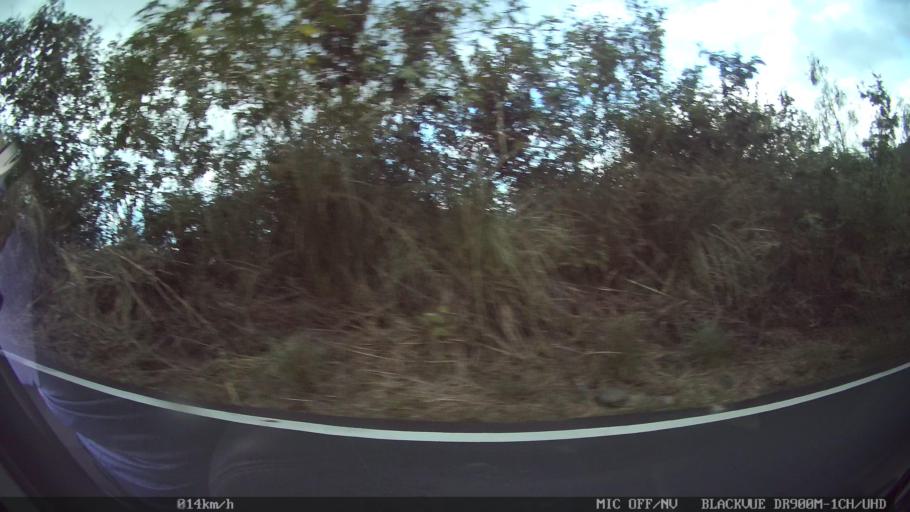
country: ID
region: Bali
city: Banjar Kedisan
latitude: -8.2603
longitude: 115.3471
